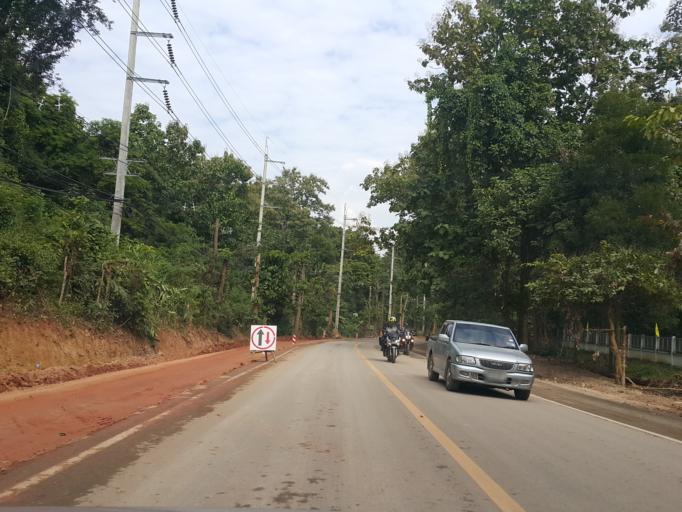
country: TH
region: Mae Hong Son
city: Mae Hong Son
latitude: 19.3233
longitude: 97.9660
